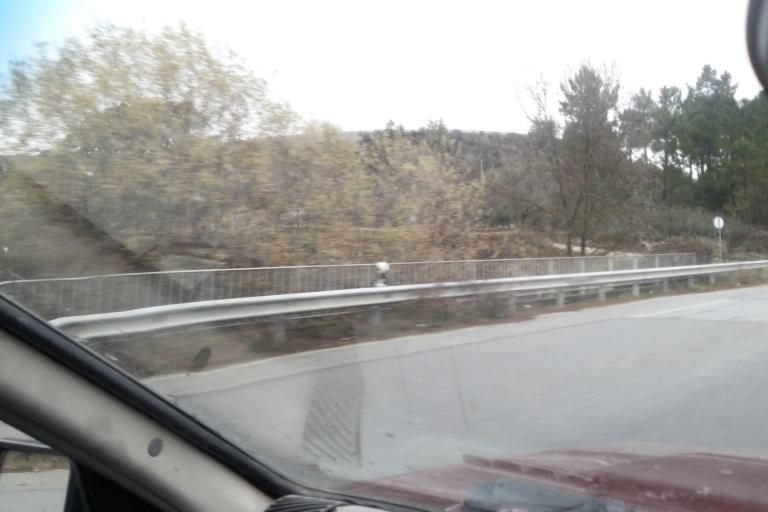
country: PT
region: Guarda
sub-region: Fornos de Algodres
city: Fornos de Algodres
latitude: 40.6055
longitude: -7.5399
